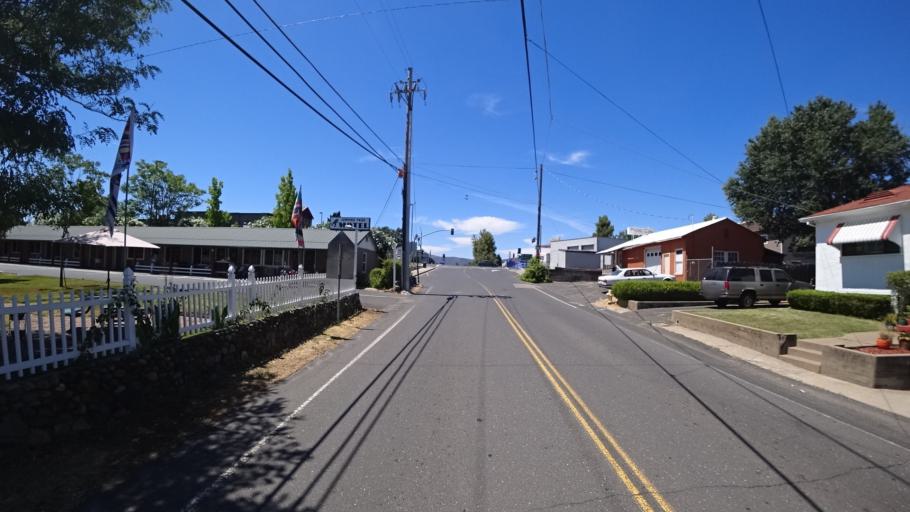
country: US
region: California
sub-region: Calaveras County
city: Angels Camp
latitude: 38.0800
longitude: -120.5539
